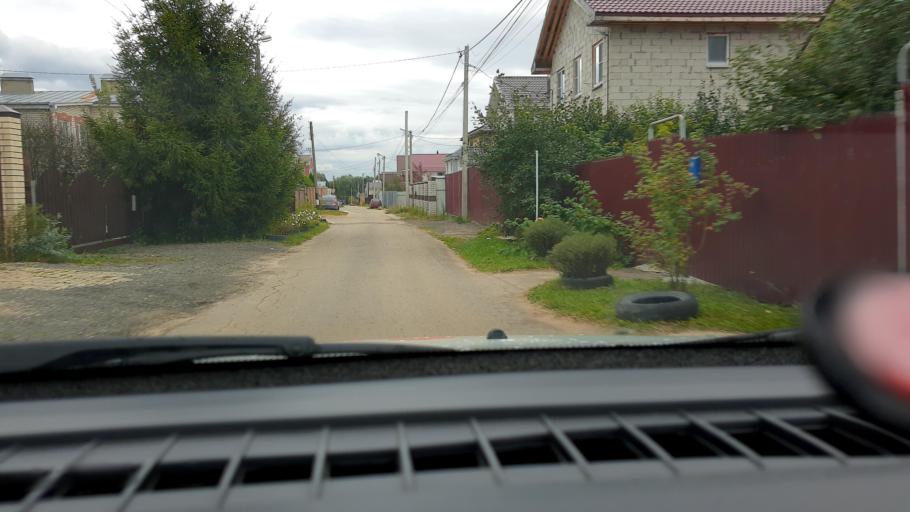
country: RU
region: Nizjnij Novgorod
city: Afonino
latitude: 56.2047
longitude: 44.1000
